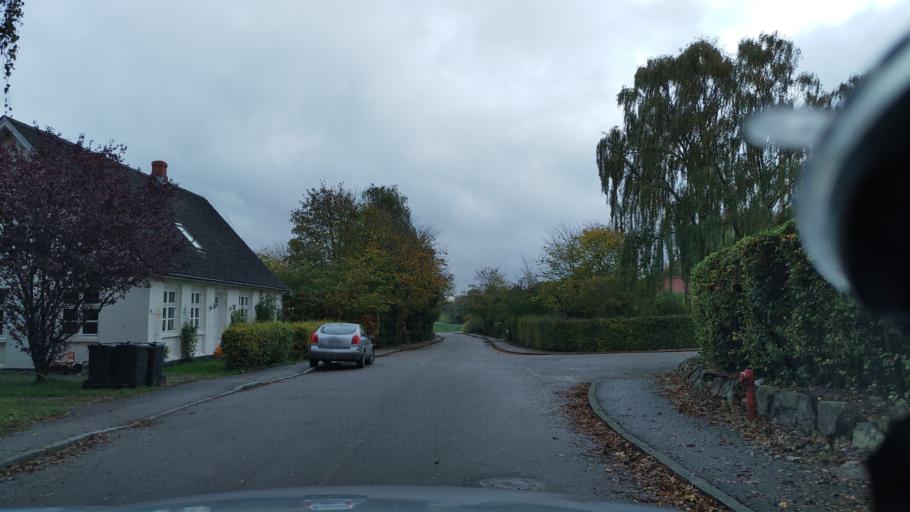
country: DK
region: Zealand
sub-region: Faxe Kommune
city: Ronnede
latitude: 55.2655
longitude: 11.9640
